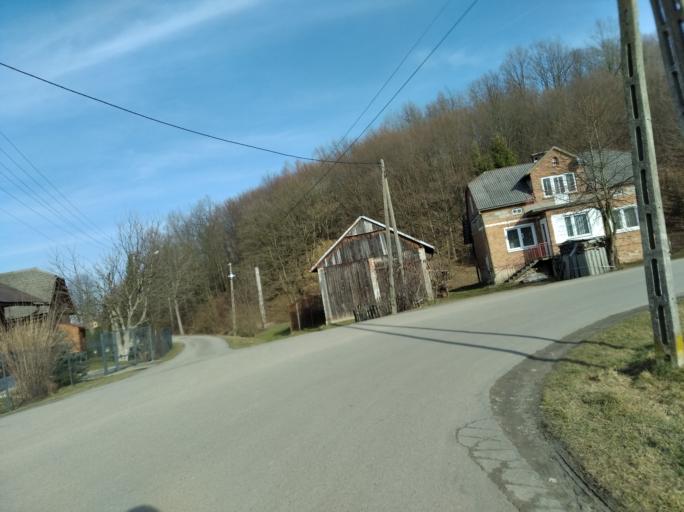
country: PL
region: Subcarpathian Voivodeship
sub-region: Powiat brzozowski
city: Gorki
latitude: 49.6431
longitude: 22.0505
